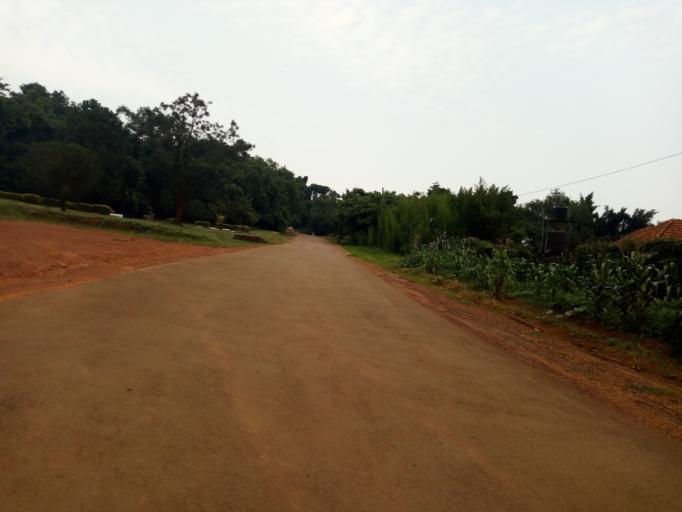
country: UG
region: Central Region
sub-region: Wakiso District
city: Kireka
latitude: 0.3281
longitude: 32.6265
